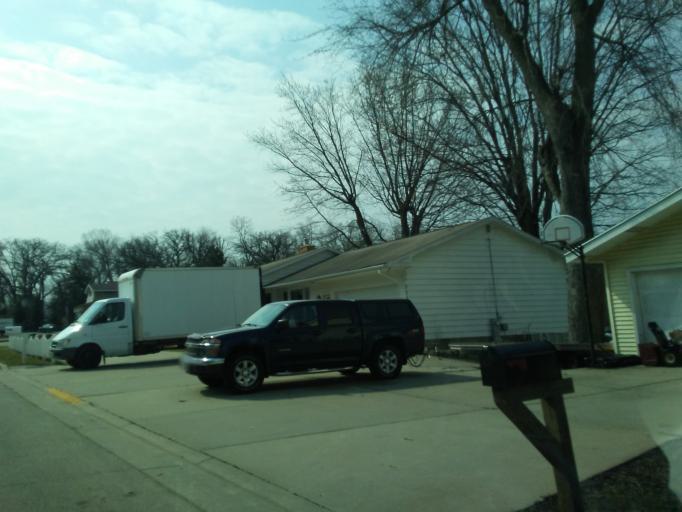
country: US
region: Wisconsin
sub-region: Columbia County
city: Lodi
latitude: 43.3092
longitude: -89.5264
